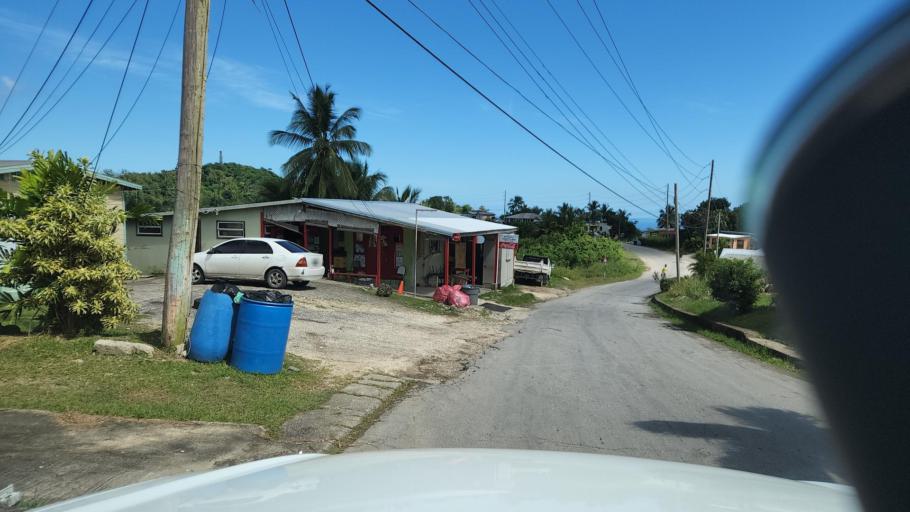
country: BB
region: Saint Thomas
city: Welchman Hall
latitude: 13.2085
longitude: -59.5559
